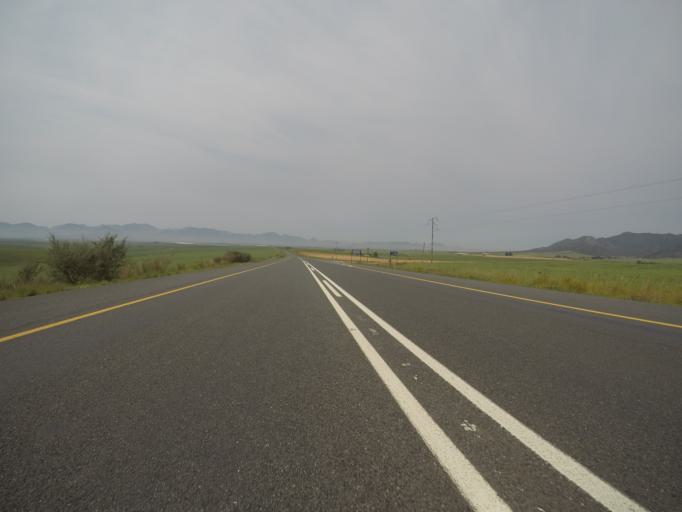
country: ZA
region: Western Cape
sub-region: West Coast District Municipality
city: Malmesbury
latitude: -33.5392
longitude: 18.8575
